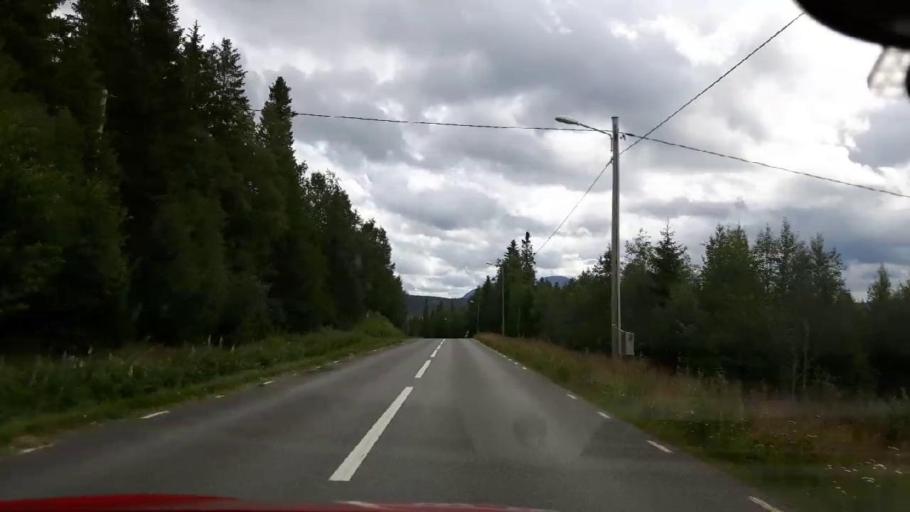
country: NO
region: Nord-Trondelag
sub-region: Lierne
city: Sandvika
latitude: 64.3922
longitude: 14.3707
